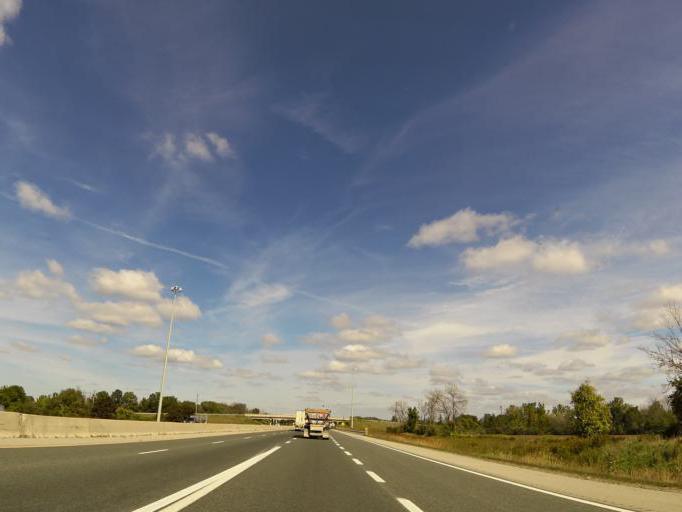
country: CA
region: Ontario
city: London
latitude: 42.9100
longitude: -81.2270
